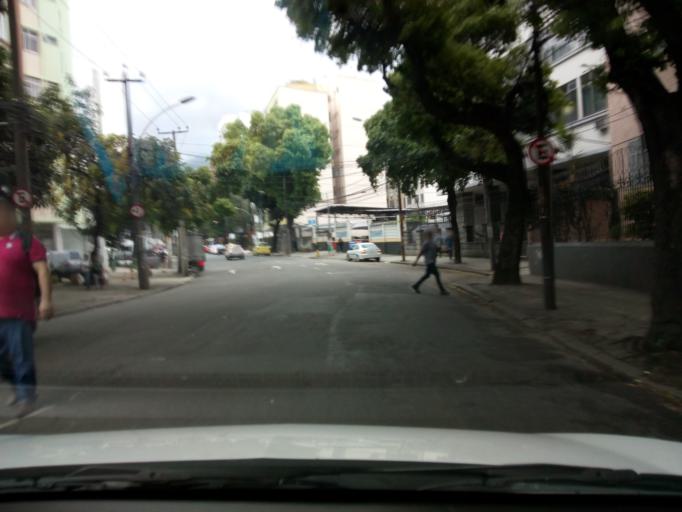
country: BR
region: Rio de Janeiro
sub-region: Rio De Janeiro
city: Rio de Janeiro
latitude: -22.9220
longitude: -43.2302
